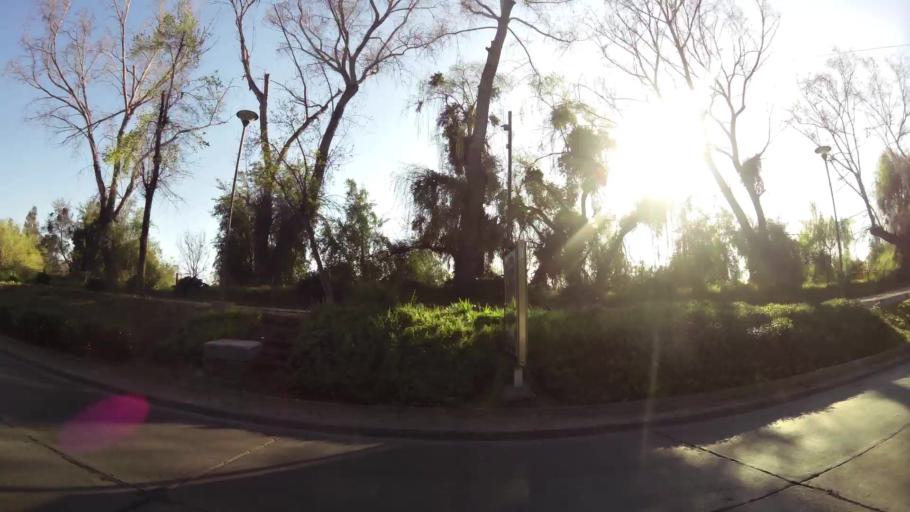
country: CL
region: Santiago Metropolitan
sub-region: Provincia de Santiago
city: Villa Presidente Frei, Nunoa, Santiago, Chile
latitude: -33.4463
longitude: -70.5653
